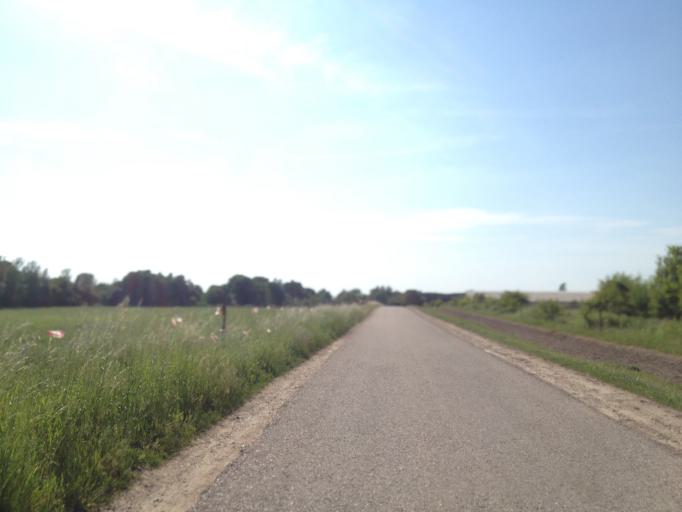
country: DK
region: Capital Region
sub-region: Ballerup Kommune
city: Ballerup
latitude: 55.7062
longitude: 12.3306
